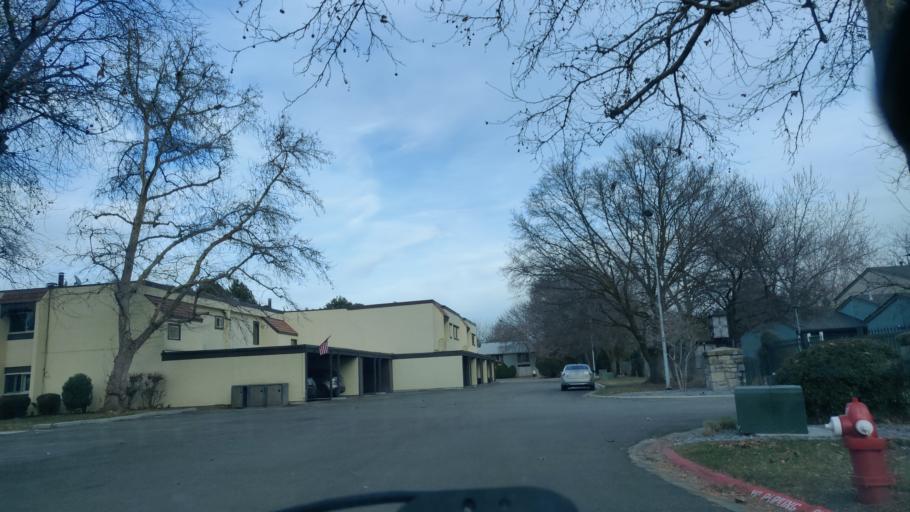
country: US
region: Idaho
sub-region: Ada County
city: Garden City
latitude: 43.6144
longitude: -116.2707
